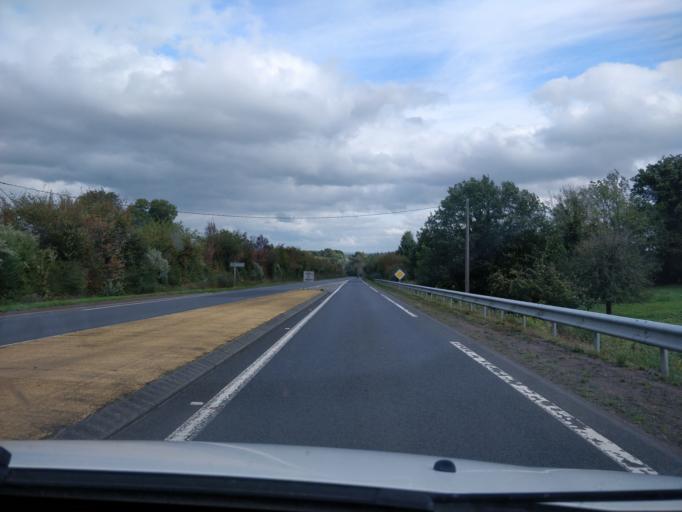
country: FR
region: Lower Normandy
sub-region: Departement du Calvados
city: Saint-Sever-Calvados
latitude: 48.8381
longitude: -1.0253
